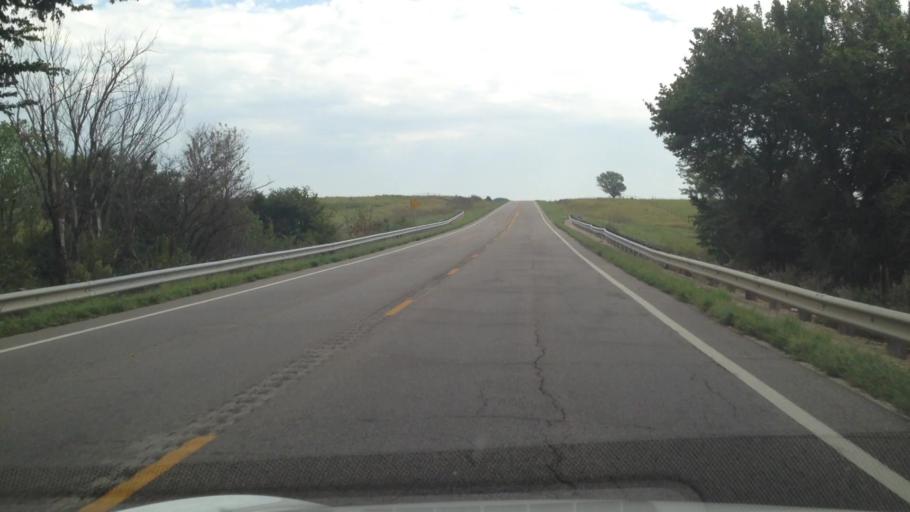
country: US
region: Kansas
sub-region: Bourbon County
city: Fort Scott
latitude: 37.8864
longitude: -95.0254
